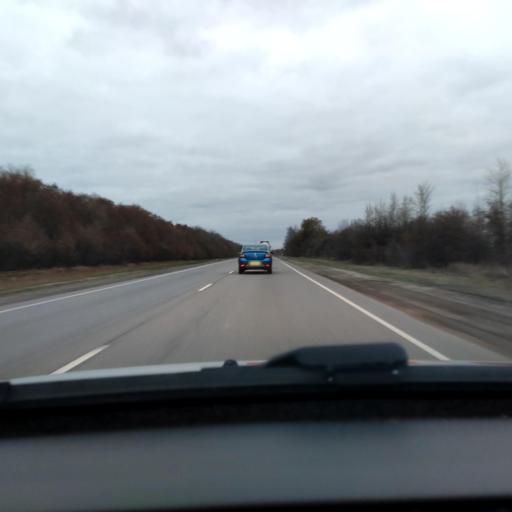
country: RU
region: Lipetsk
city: Borinskoye
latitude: 52.4296
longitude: 39.2652
